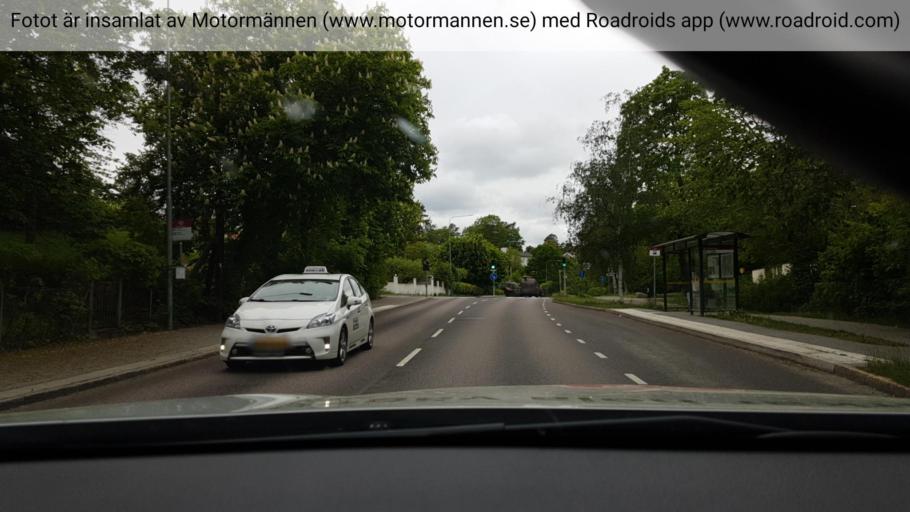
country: SE
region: Stockholm
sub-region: Lidingo
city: Lidingoe
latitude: 59.3631
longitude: 18.1454
